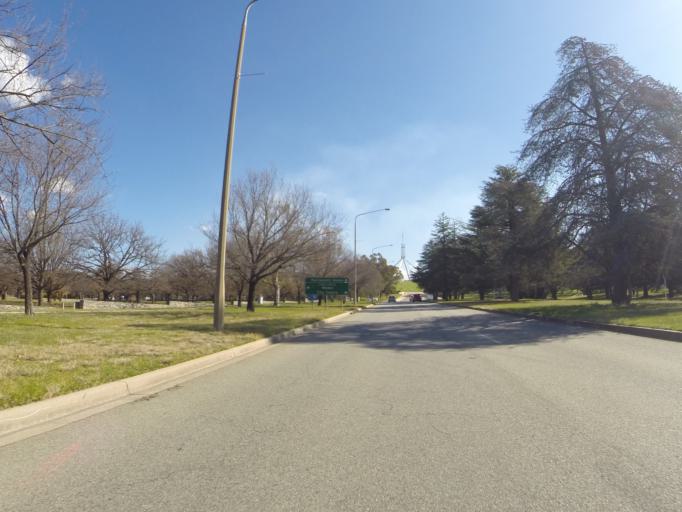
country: AU
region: Australian Capital Territory
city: Forrest
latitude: -35.3058
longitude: 149.1309
